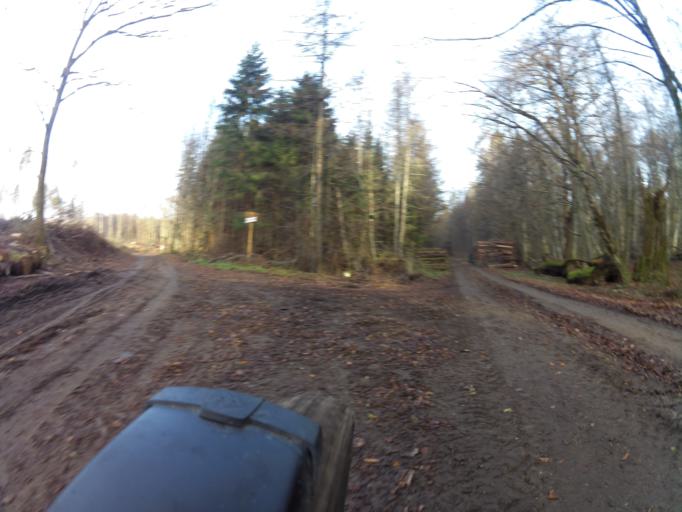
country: PL
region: West Pomeranian Voivodeship
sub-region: Powiat koszalinski
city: Polanow
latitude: 54.1630
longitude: 16.7295
